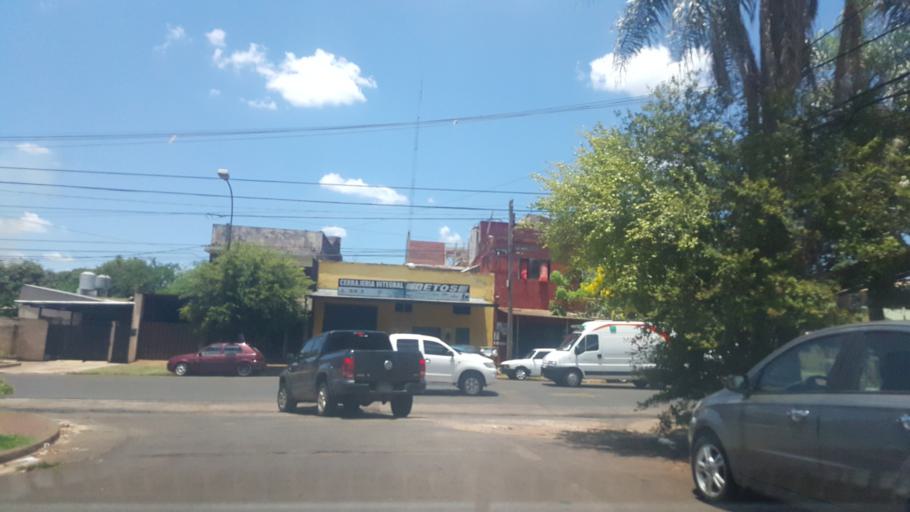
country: AR
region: Misiones
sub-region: Departamento de Capital
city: Posadas
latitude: -27.3834
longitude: -55.9055
